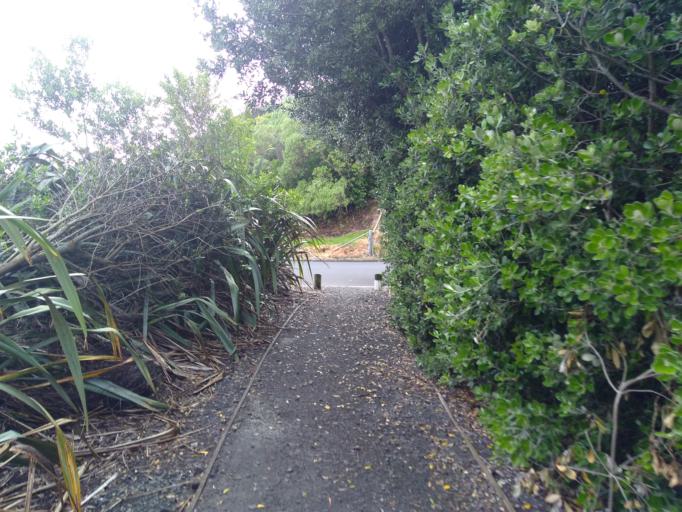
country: NZ
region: Auckland
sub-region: Auckland
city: Mangere
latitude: -36.9791
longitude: 174.7626
